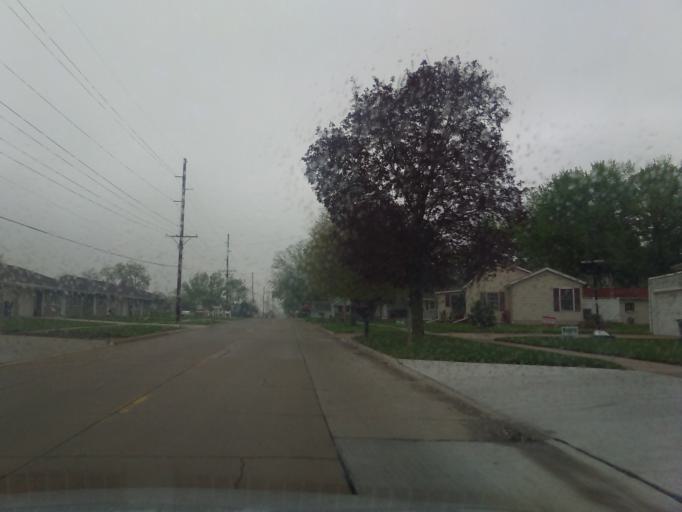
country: US
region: Nebraska
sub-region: Madison County
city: Norfolk
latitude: 42.0425
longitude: -97.4192
